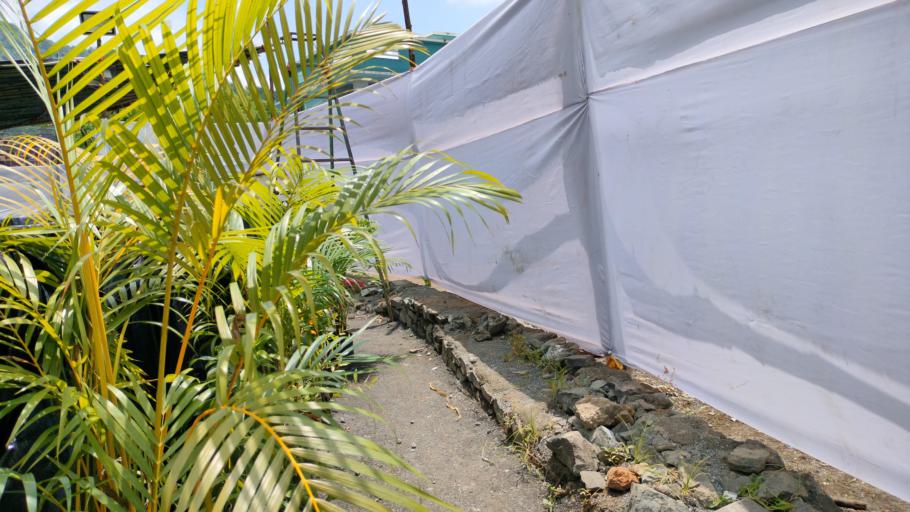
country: IN
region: Maharashtra
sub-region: Thane
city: Virar
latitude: 19.4770
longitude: 72.8257
